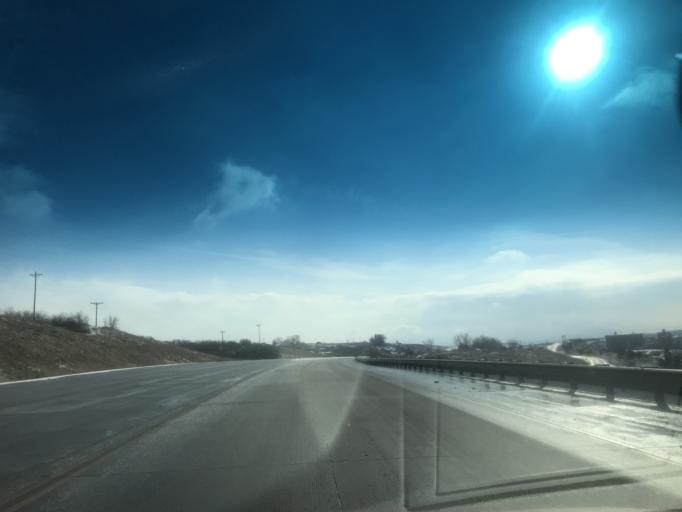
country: US
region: Colorado
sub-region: Douglas County
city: Castle Pines
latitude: 39.4523
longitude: -104.9775
